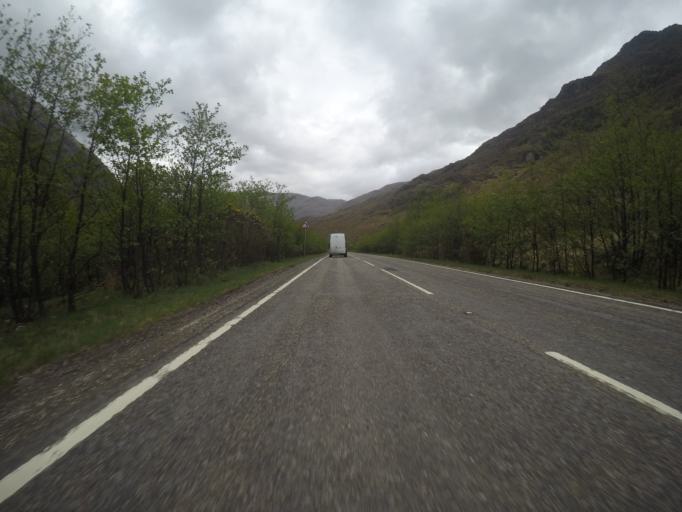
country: GB
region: Scotland
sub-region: Highland
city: Fort William
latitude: 57.1838
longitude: -5.3821
